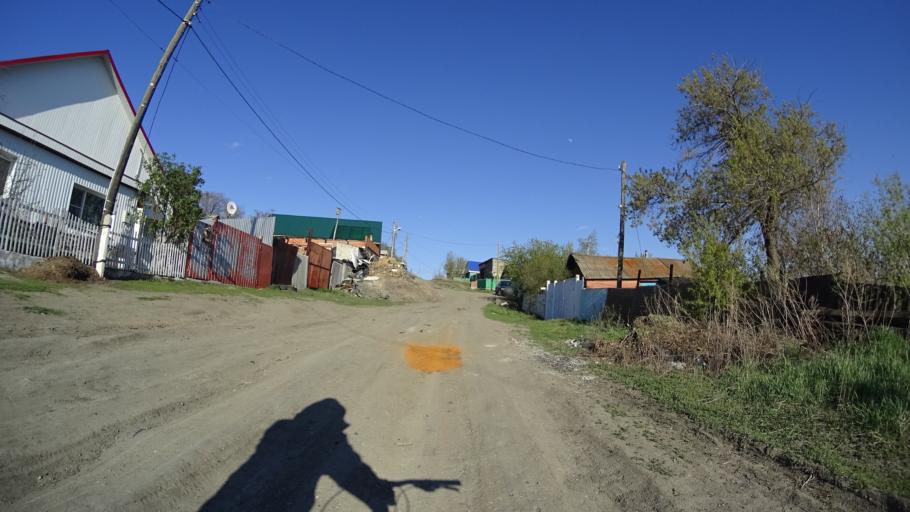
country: RU
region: Chelyabinsk
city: Troitsk
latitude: 54.0985
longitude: 61.5517
